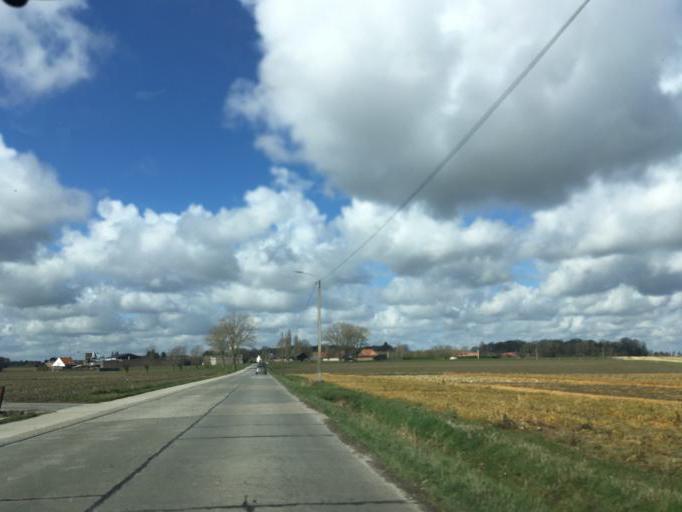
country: BE
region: Flanders
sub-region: Provincie West-Vlaanderen
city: Ledegem
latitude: 50.9015
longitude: 3.1093
